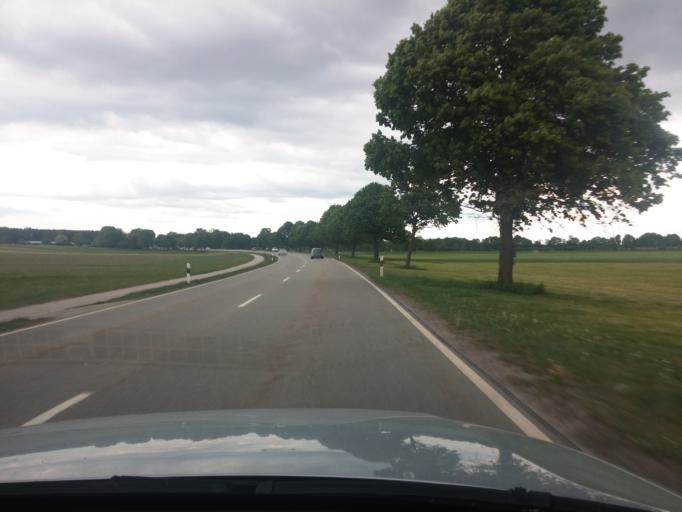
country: DE
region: Bavaria
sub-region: Upper Bavaria
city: Holzkirchen
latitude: 47.8575
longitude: 11.6874
